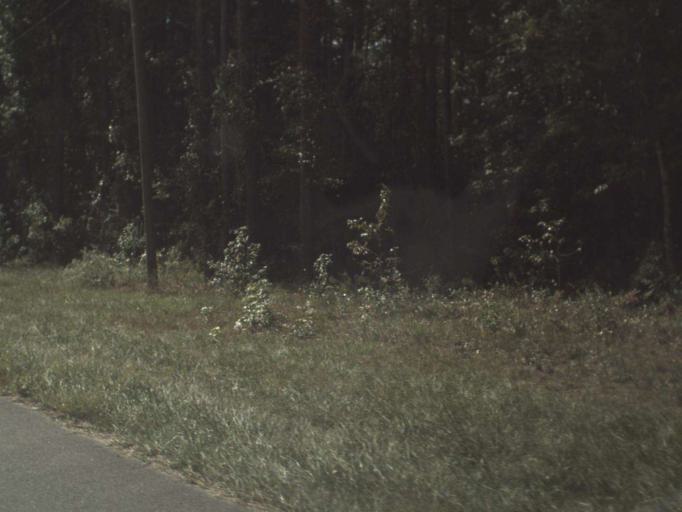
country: US
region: Florida
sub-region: Holmes County
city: Bonifay
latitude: 30.7142
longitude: -85.6171
